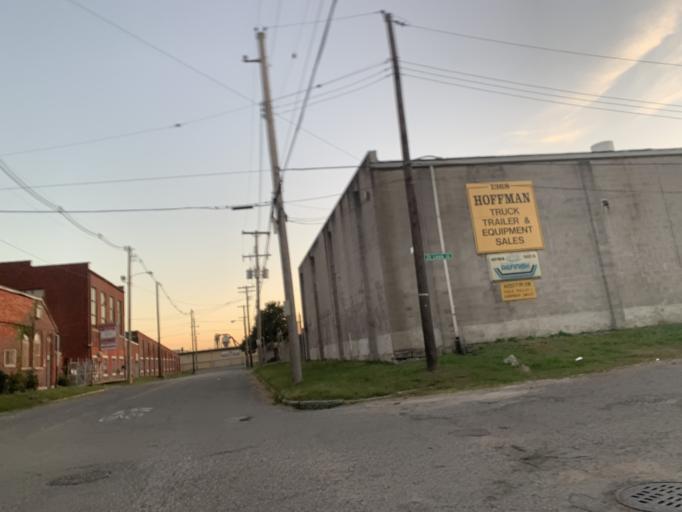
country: US
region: Kentucky
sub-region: Jefferson County
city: Louisville
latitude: 38.2315
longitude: -85.7725
